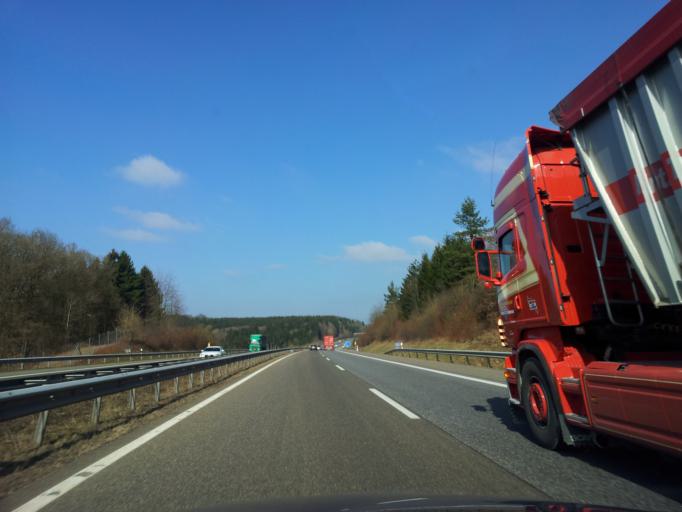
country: DE
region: Rheinland-Pfalz
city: Orlenbach
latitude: 50.1598
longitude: 6.3951
